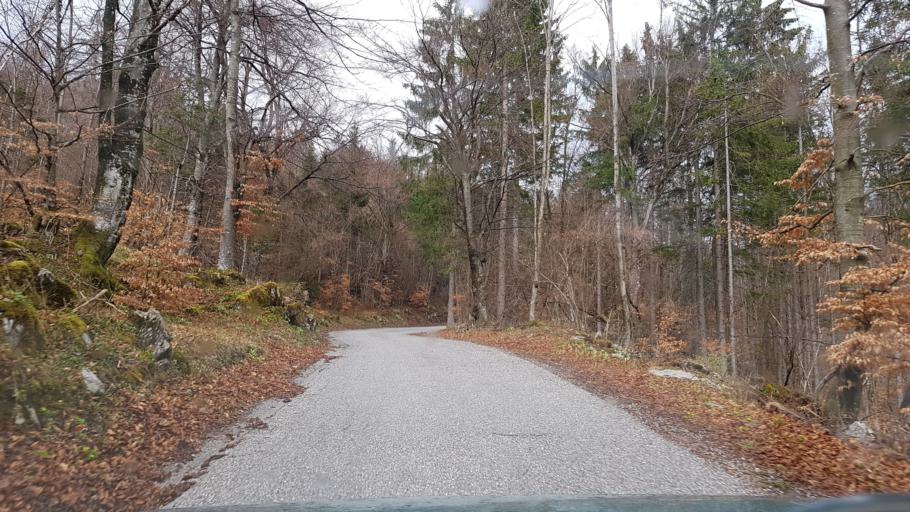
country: SI
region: Cerkno
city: Cerkno
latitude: 46.1312
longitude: 13.8737
